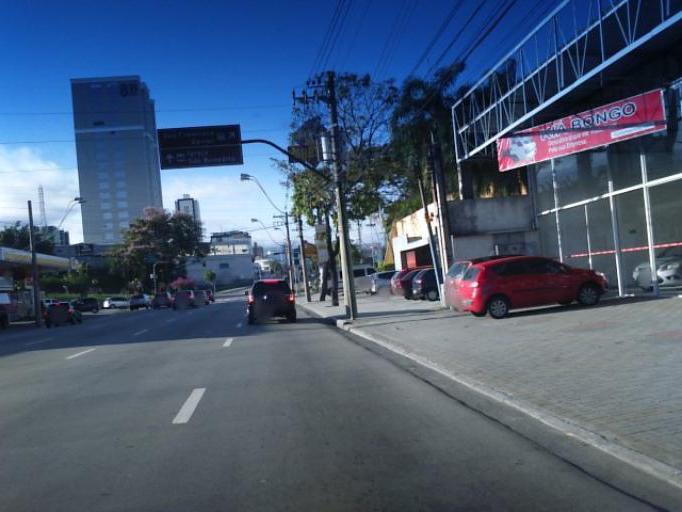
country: BR
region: Sao Paulo
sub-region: Sao Jose Dos Campos
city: Sao Jose dos Campos
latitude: -23.2011
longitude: -45.8854
